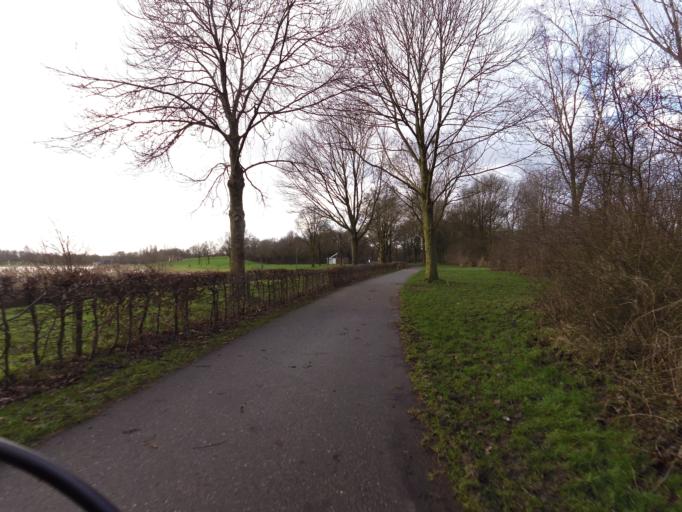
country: NL
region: Gelderland
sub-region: Gemeente Doetinchem
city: Doetinchem
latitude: 51.9371
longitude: 6.2634
